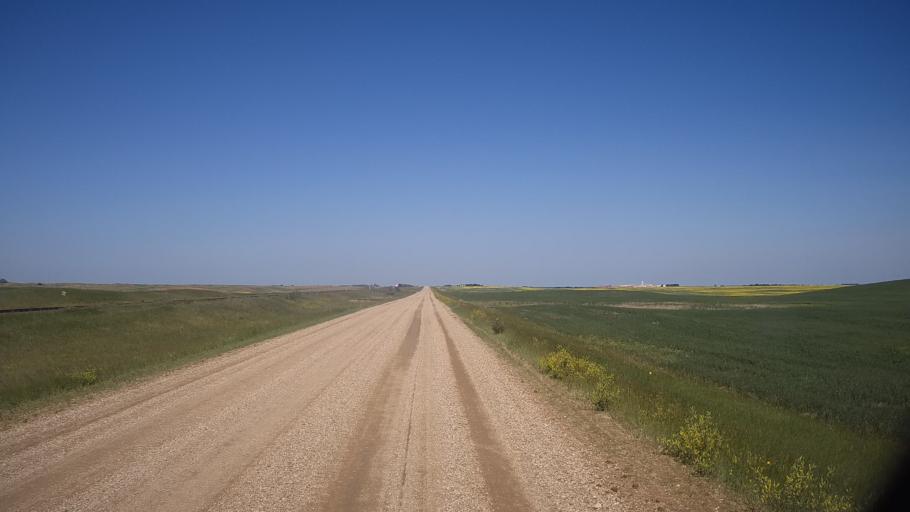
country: CA
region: Saskatchewan
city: Watrous
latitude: 51.8531
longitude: -105.9417
